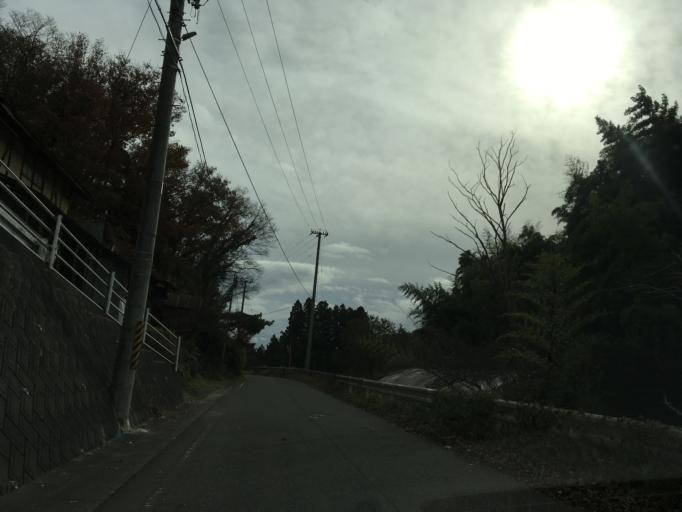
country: JP
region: Iwate
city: Ichinoseki
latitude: 38.7712
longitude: 141.2688
